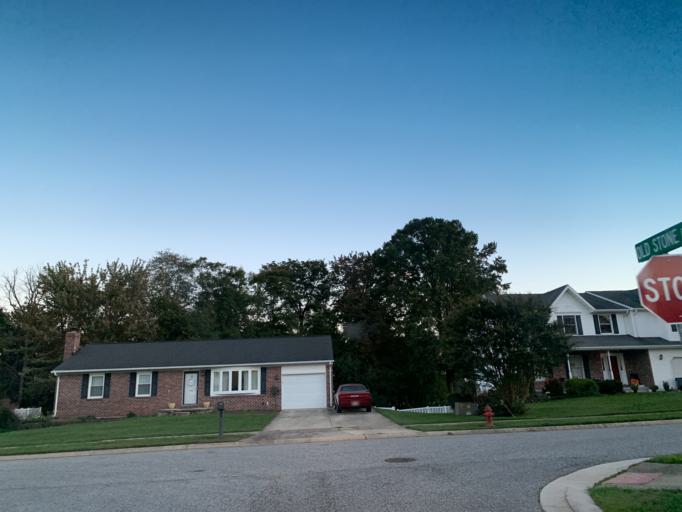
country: US
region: Maryland
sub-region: Harford County
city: South Bel Air
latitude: 39.5442
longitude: -76.3014
